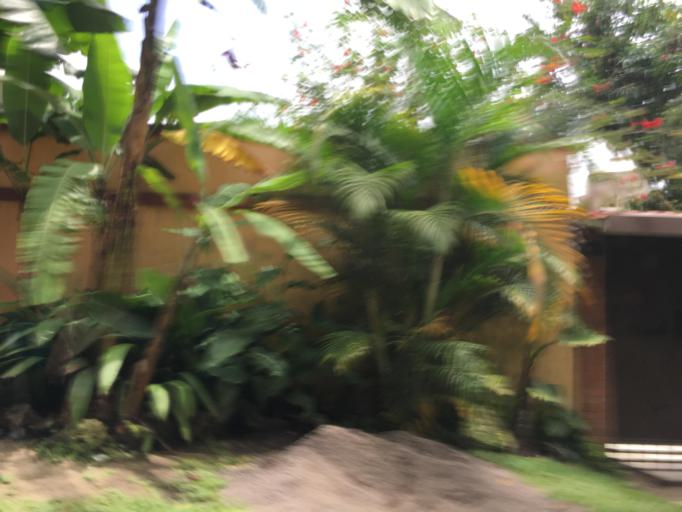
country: GT
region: Guatemala
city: Villa Canales
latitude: 14.4224
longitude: -90.5355
